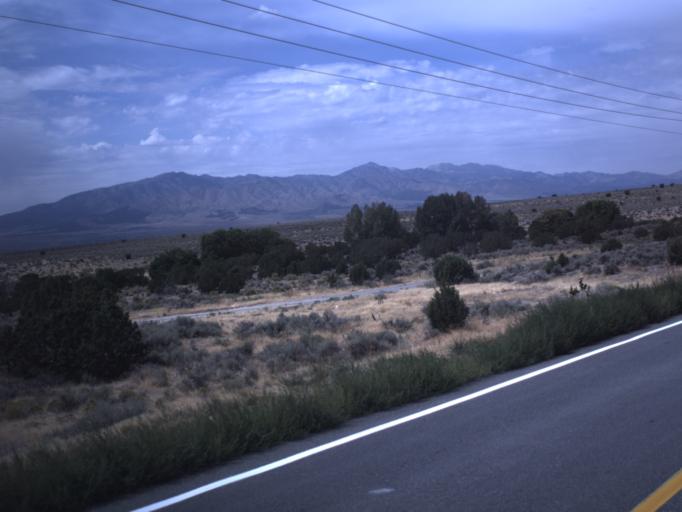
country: US
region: Utah
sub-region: Tooele County
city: Tooele
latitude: 40.3407
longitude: -112.3028
